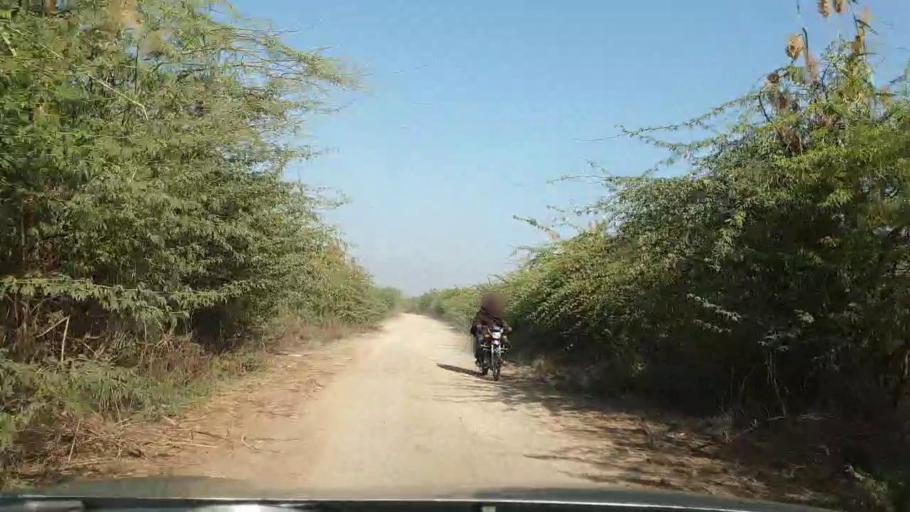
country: PK
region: Sindh
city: Mirpur Khas
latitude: 25.6563
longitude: 68.9132
